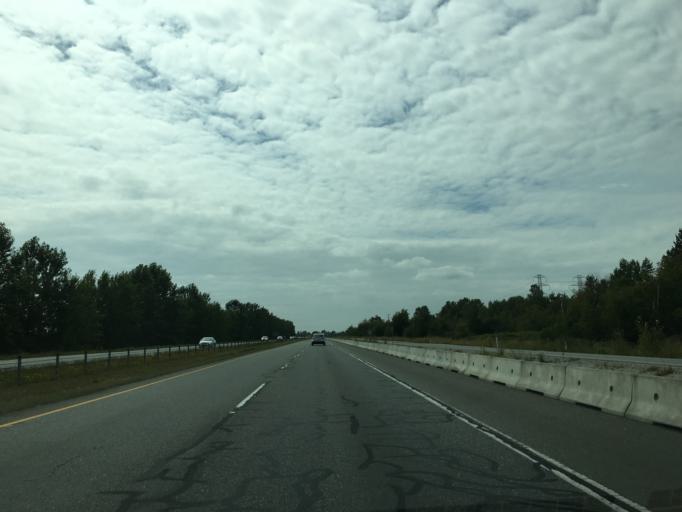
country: CA
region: British Columbia
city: Ladner
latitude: 49.0906
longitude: -122.9880
